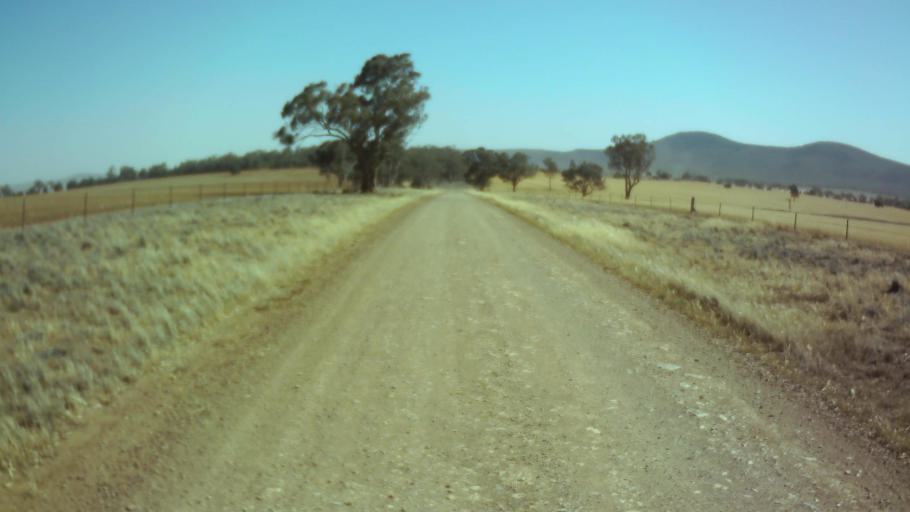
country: AU
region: New South Wales
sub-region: Weddin
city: Grenfell
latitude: -33.8524
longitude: 148.0162
